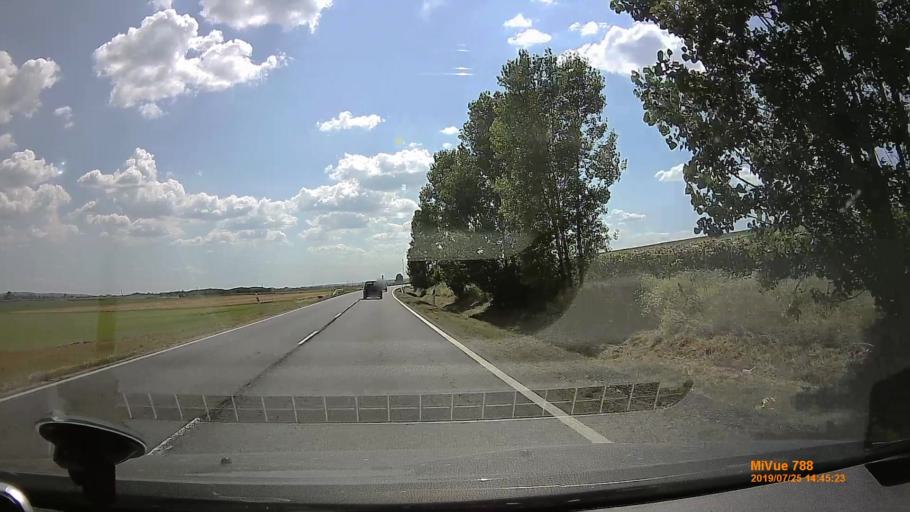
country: HU
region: Borsod-Abauj-Zemplen
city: Halmaj
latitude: 48.2600
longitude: 20.9912
